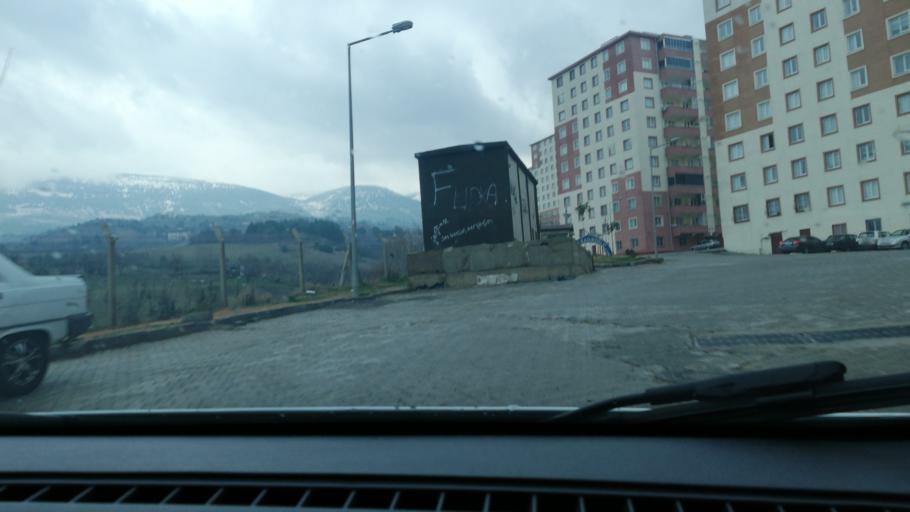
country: TR
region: Kahramanmaras
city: Kahramanmaras
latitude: 37.5801
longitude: 36.9977
